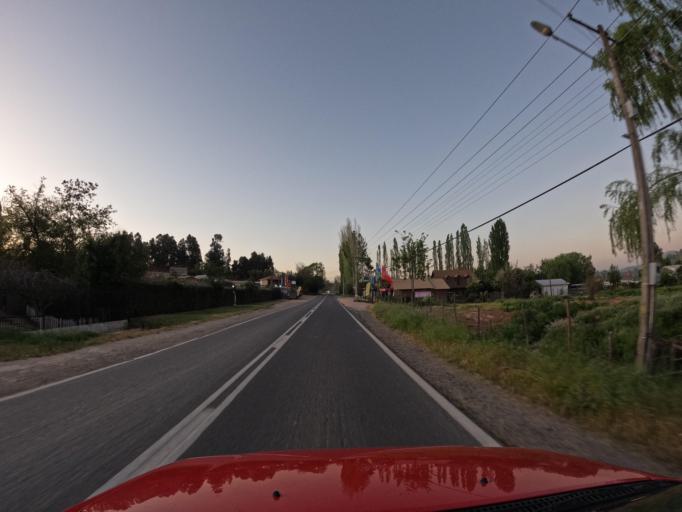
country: CL
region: O'Higgins
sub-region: Provincia de Cachapoal
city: San Vicente
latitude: -34.1695
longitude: -71.4074
